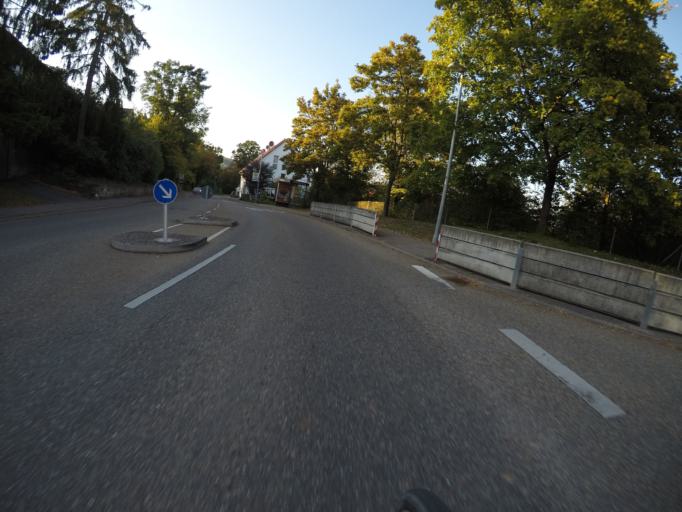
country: DE
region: Baden-Wuerttemberg
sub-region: Regierungsbezirk Stuttgart
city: Ostfildern
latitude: 48.7518
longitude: 9.2419
